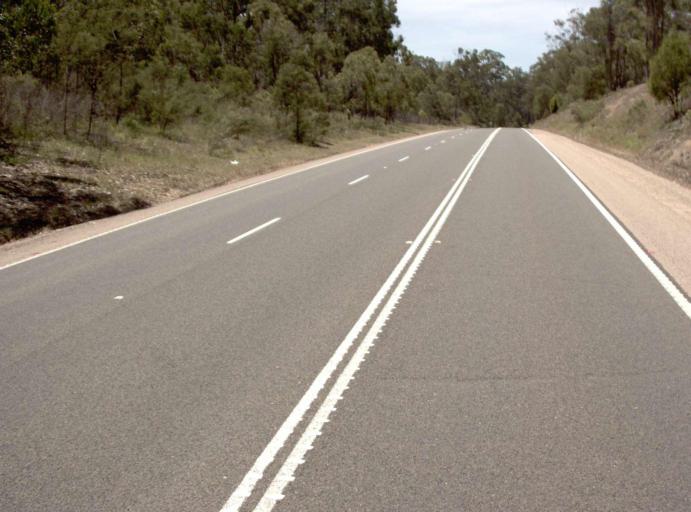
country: AU
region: Victoria
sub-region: East Gippsland
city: Bairnsdale
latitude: -37.7401
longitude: 147.7660
